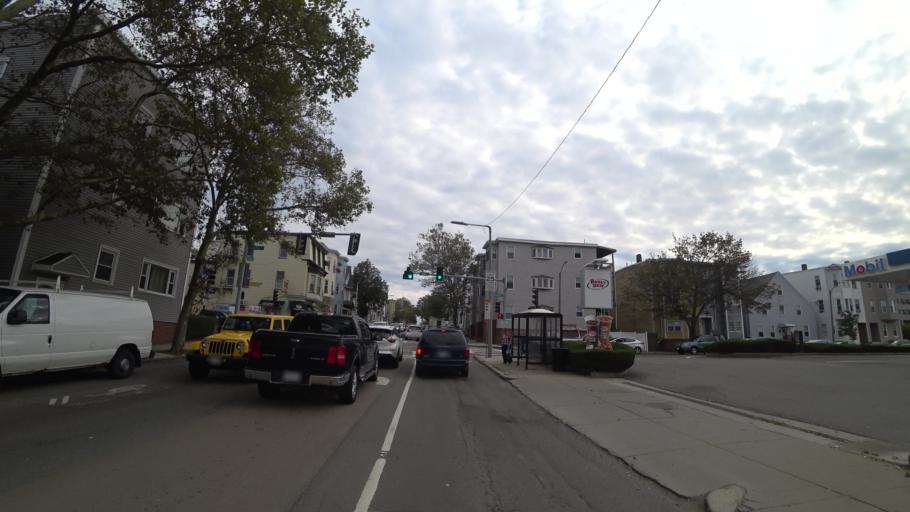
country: US
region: Massachusetts
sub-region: Suffolk County
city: Chelsea
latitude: 42.3829
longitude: -71.0393
